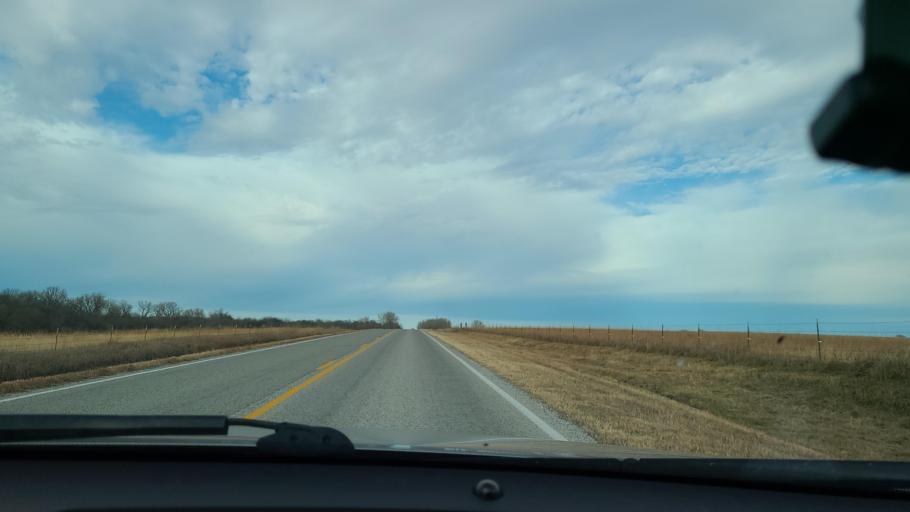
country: US
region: Kansas
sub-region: McPherson County
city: Inman
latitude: 38.3406
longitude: -97.9244
